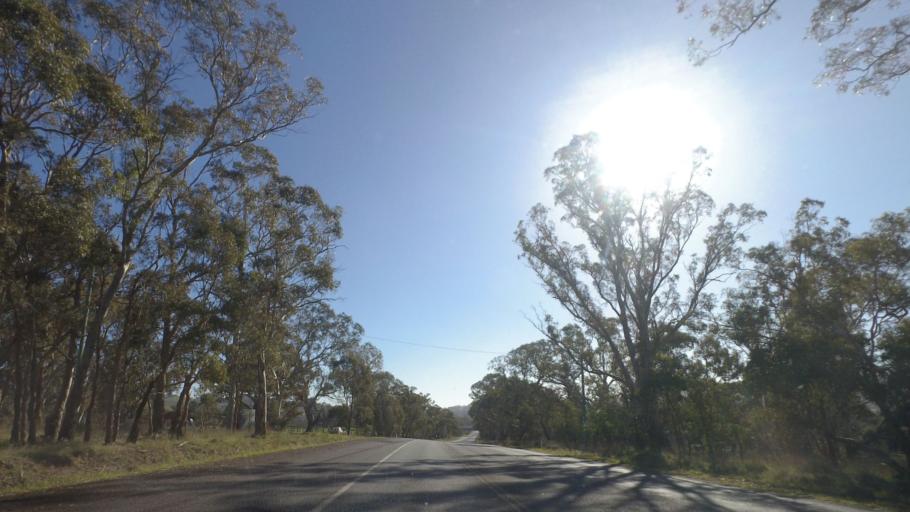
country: AU
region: Victoria
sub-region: Mount Alexander
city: Castlemaine
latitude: -37.0534
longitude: 144.2933
